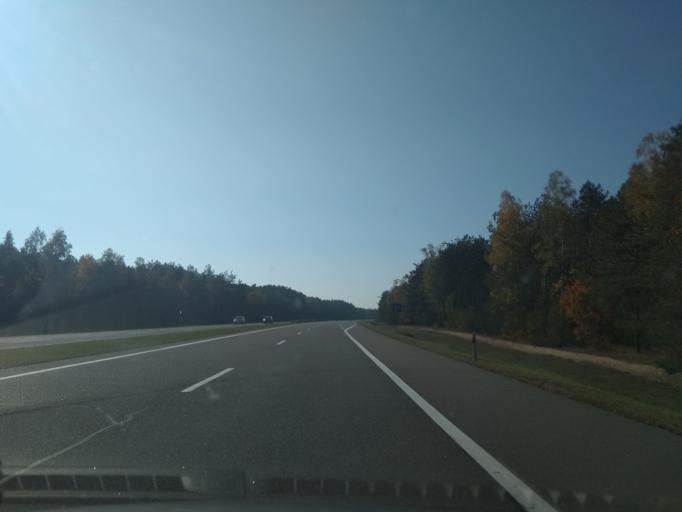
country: BY
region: Brest
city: Antopal'
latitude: 52.3667
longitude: 24.7352
